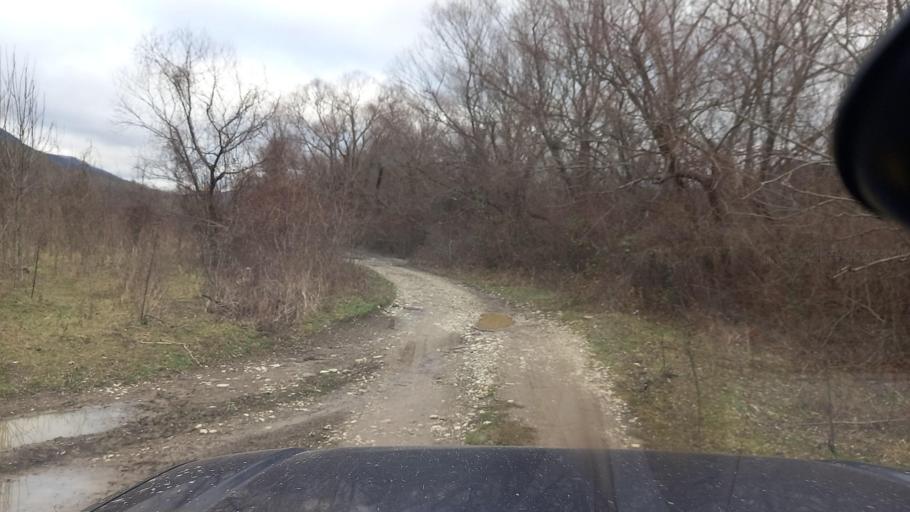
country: RU
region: Krasnodarskiy
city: Pshada
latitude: 44.4875
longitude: 38.4084
